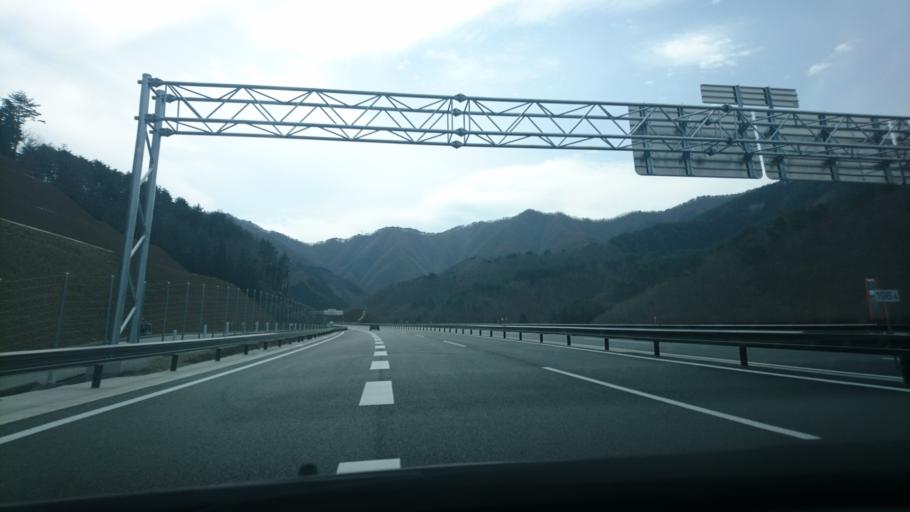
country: JP
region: Iwate
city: Kamaishi
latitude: 39.2516
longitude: 141.8374
